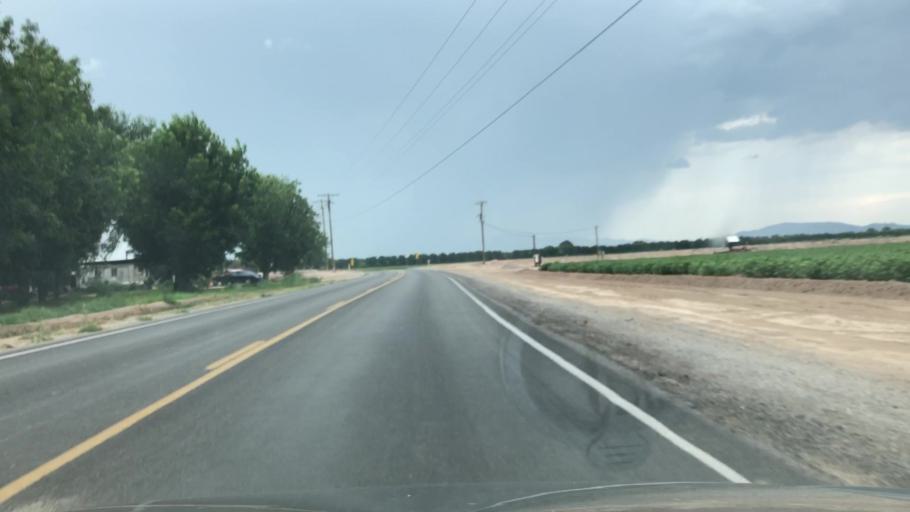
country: US
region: New Mexico
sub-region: Dona Ana County
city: La Union
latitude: 31.9731
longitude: -106.6518
